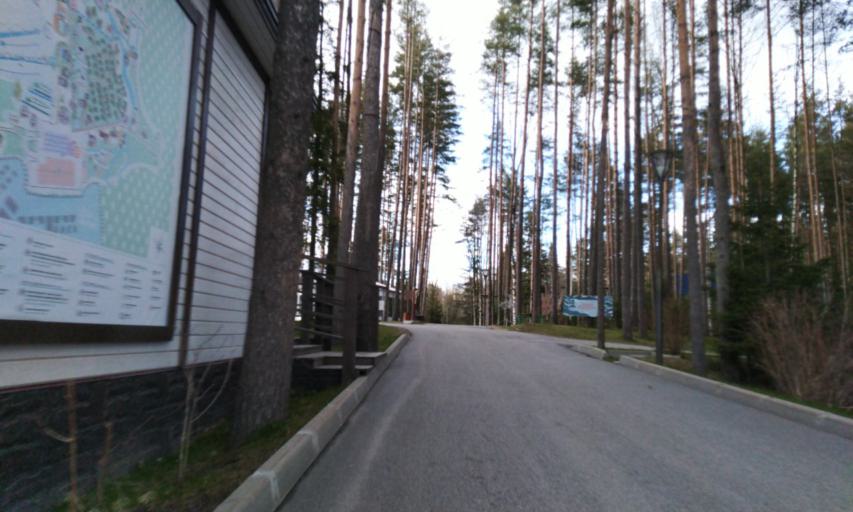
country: RU
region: Leningrad
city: Toksovo
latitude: 60.1298
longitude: 30.4450
